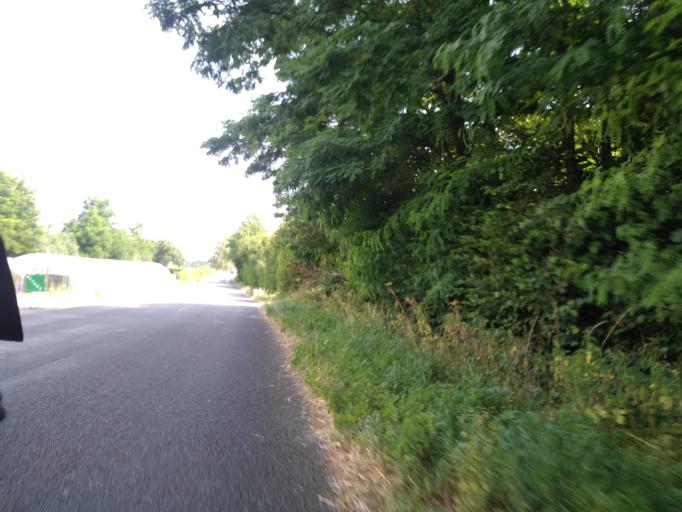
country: FR
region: Auvergne
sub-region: Departement de l'Allier
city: Molinet
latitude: 46.4623
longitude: 3.9647
